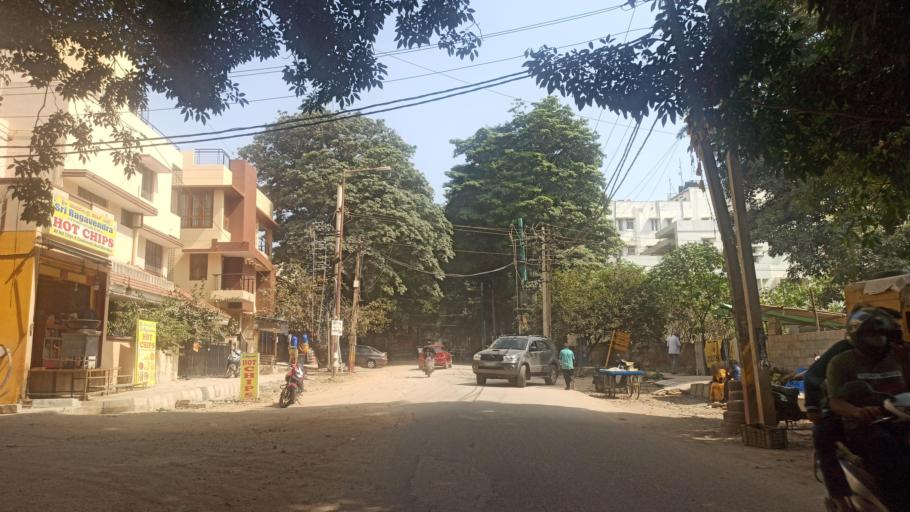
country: IN
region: Karnataka
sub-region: Bangalore Urban
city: Bangalore
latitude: 12.9637
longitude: 77.7103
